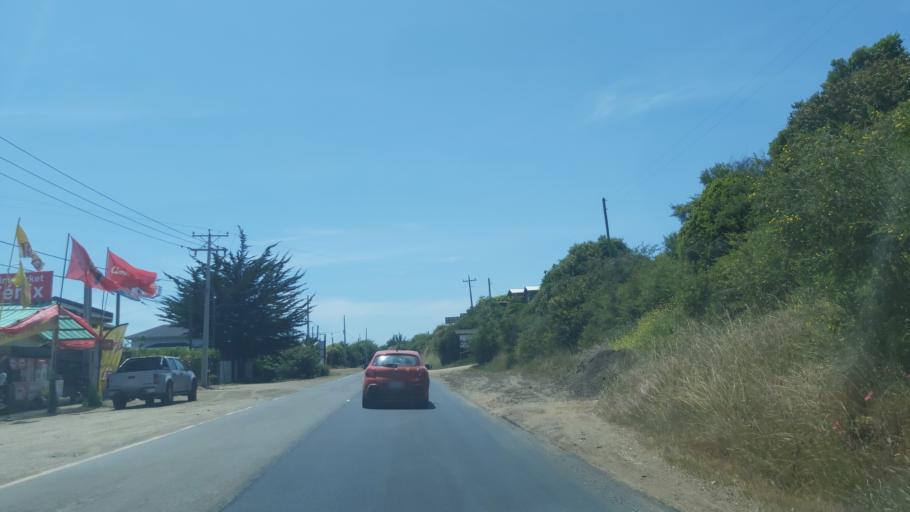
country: CL
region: Maule
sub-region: Provincia de Cauquenes
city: Cauquenes
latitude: -35.8255
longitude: -72.6059
